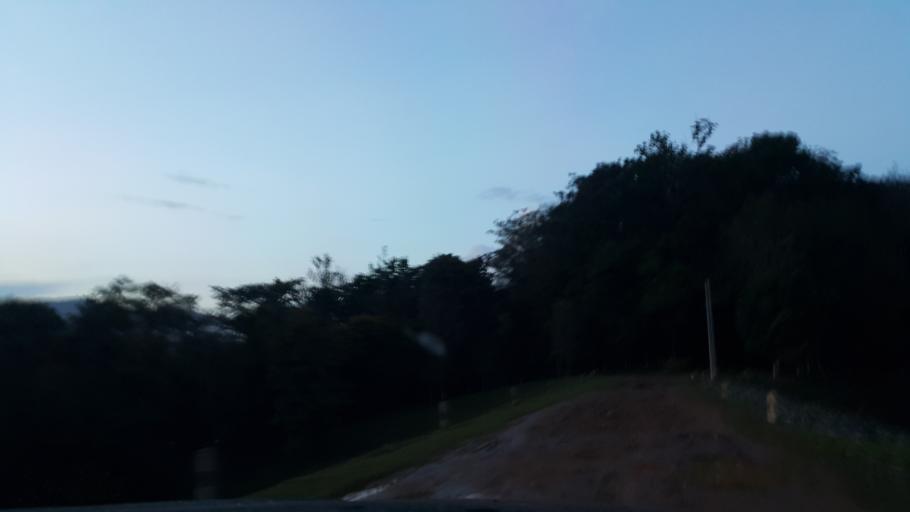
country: TH
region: Chiang Mai
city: Mae On
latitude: 18.7333
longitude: 99.3093
